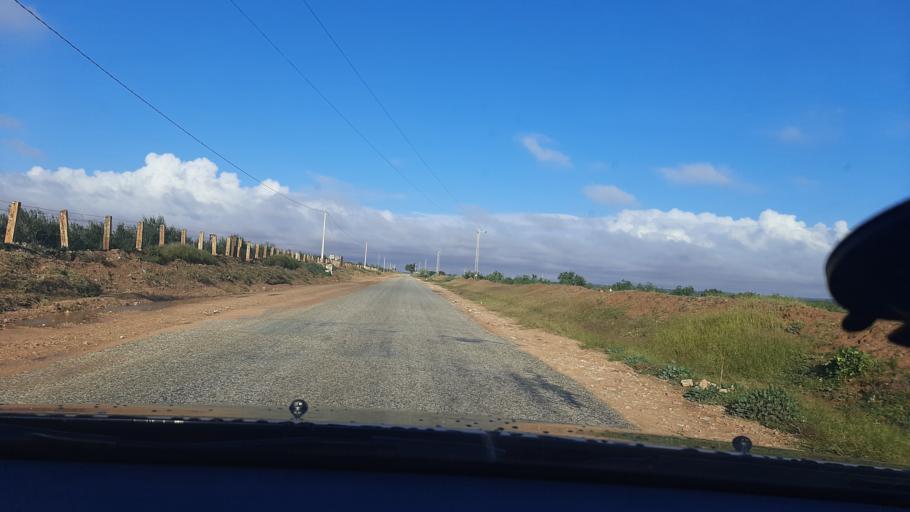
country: TN
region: Safaqis
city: Sfax
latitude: 34.8891
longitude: 10.6221
